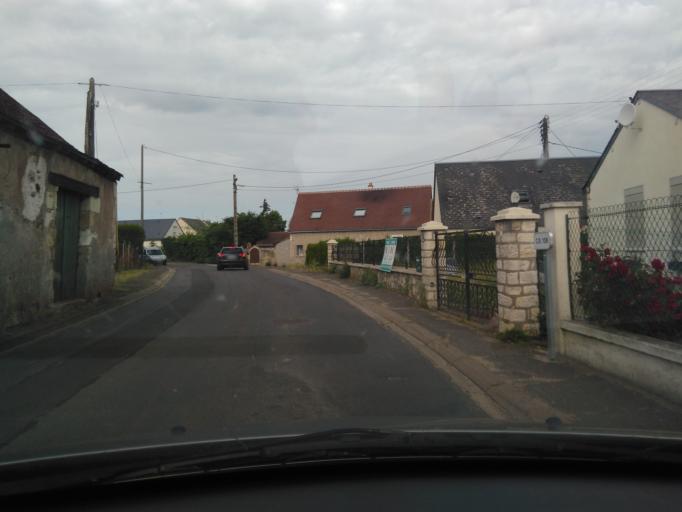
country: FR
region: Centre
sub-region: Departement d'Indre-et-Loire
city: Amboise
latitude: 47.4013
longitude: 0.9774
